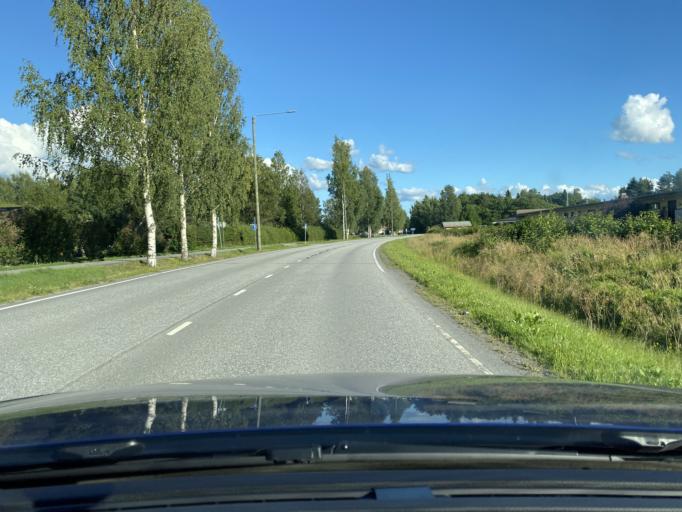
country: FI
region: Ostrobothnia
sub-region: Kyroenmaa
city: Laihia
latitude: 62.9778
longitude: 22.0014
